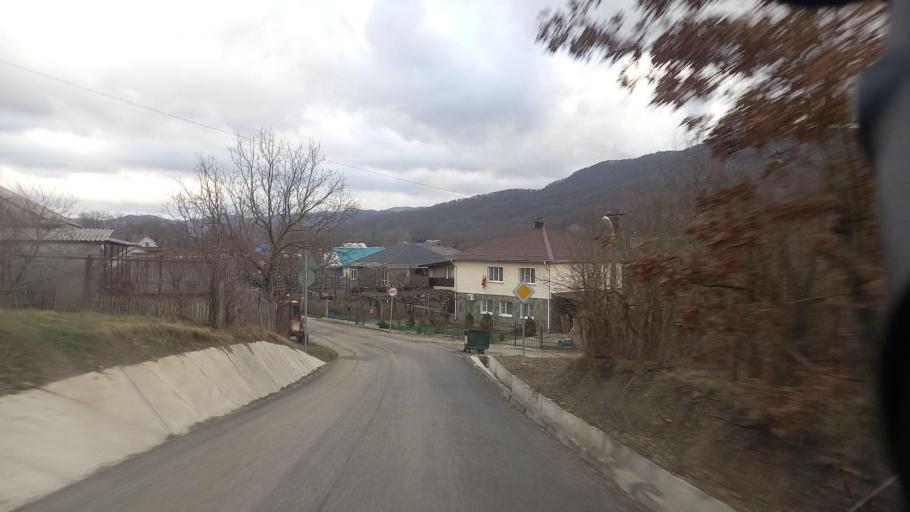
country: RU
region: Krasnodarskiy
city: Lermontovo
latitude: 44.4307
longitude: 38.7846
